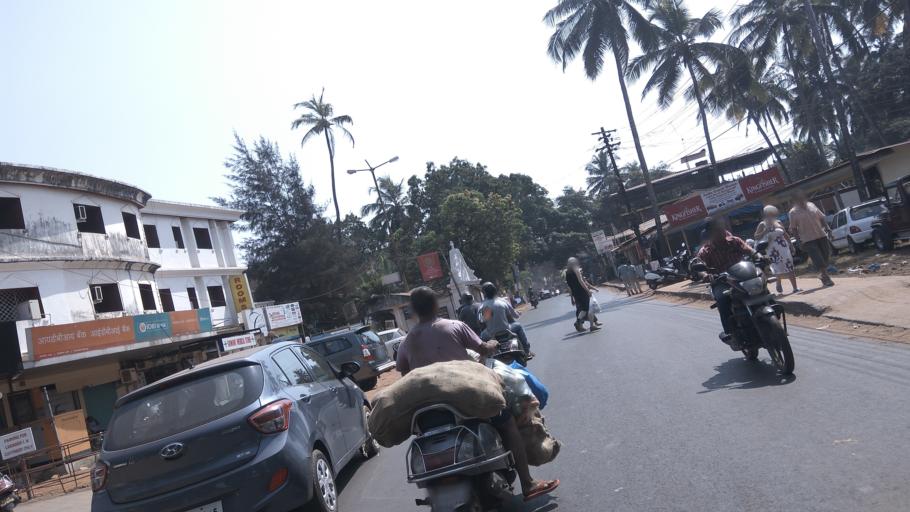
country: IN
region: Goa
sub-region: North Goa
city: Candolim
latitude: 15.5243
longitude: 73.7664
